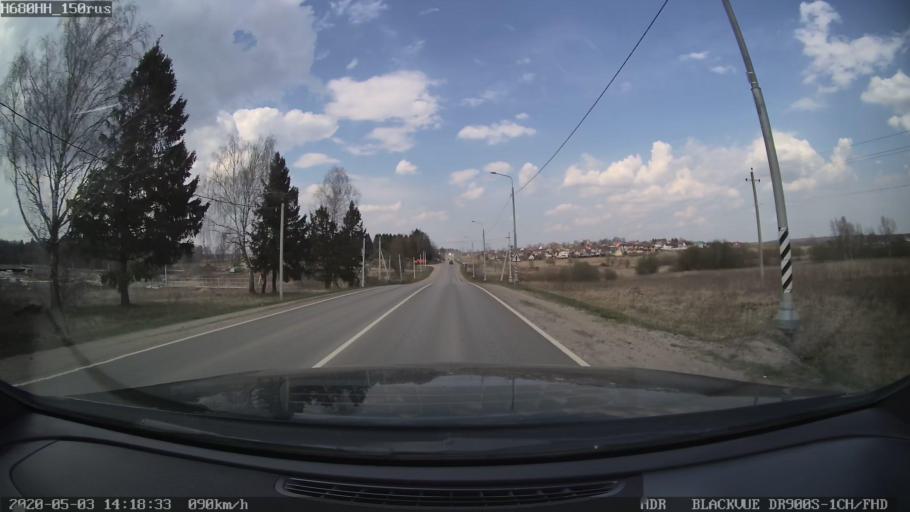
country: RU
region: Moskovskaya
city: Solnechnogorsk
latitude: 56.2207
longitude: 36.9715
